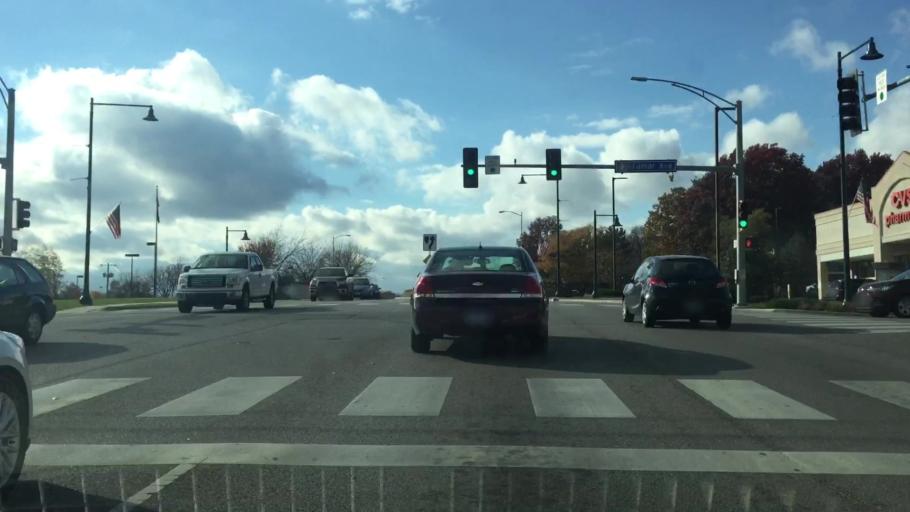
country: US
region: Kansas
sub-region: Johnson County
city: Mission
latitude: 39.0222
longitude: -94.6581
